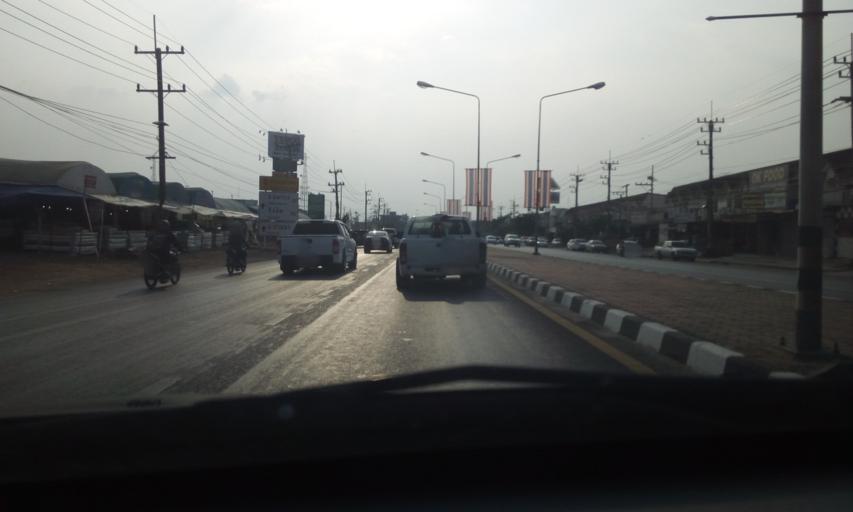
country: TH
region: Nakhon Nayok
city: Nakhon Nayok
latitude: 14.2093
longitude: 101.2191
